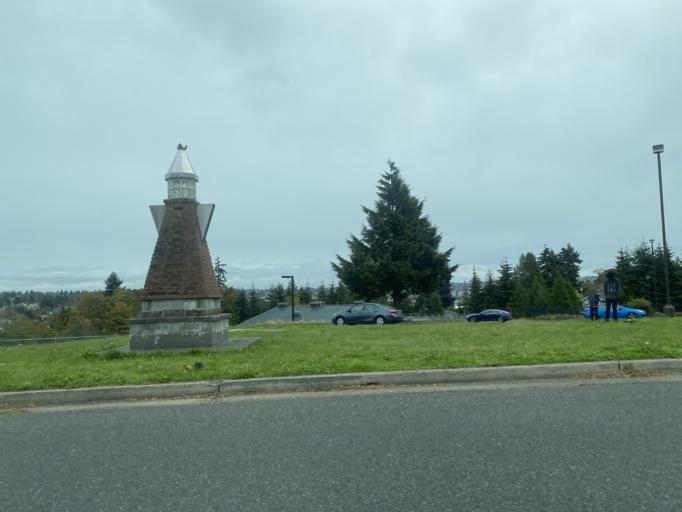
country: US
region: Washington
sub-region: King County
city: Seattle
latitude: 47.6637
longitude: -122.4058
